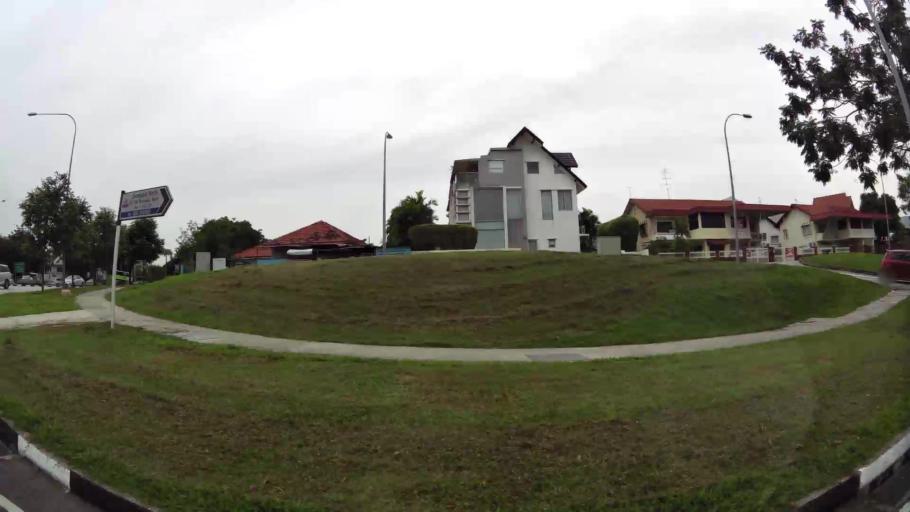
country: SG
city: Singapore
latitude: 1.3638
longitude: 103.8736
